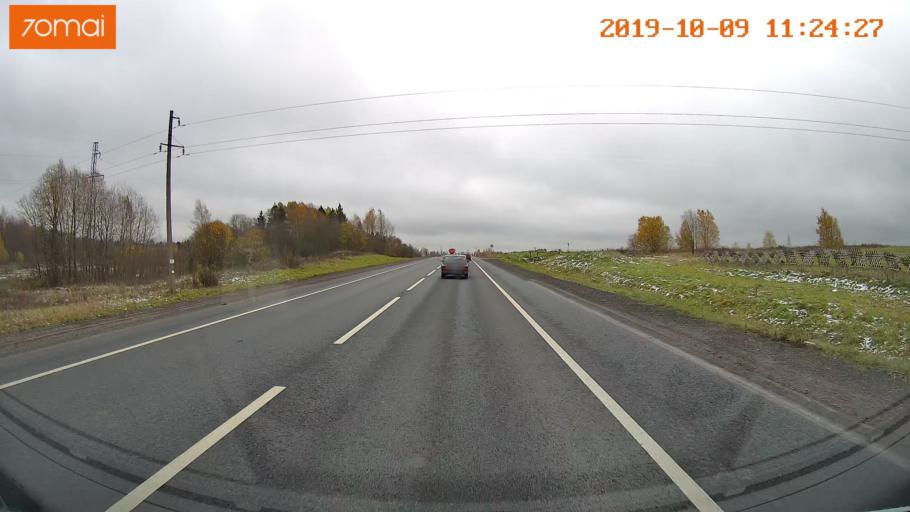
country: RU
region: Vologda
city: Vologda
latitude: 59.1114
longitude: 39.9800
